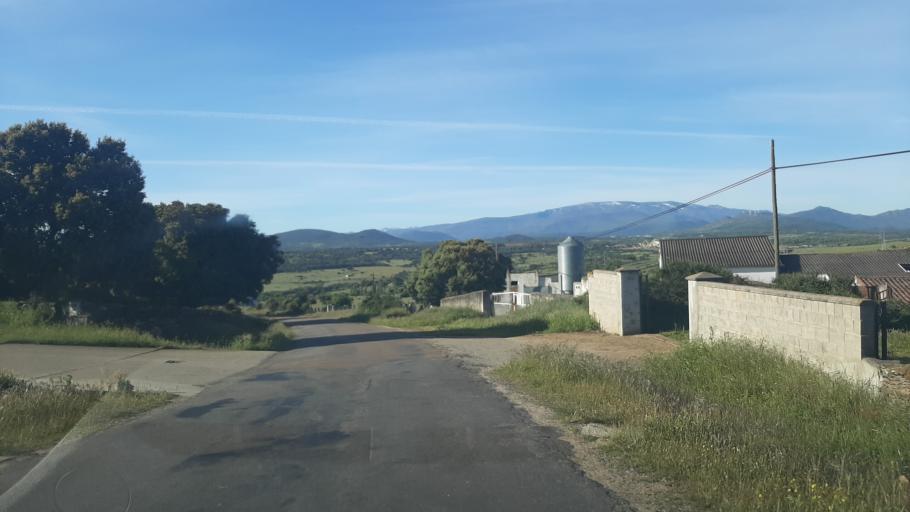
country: ES
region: Castille and Leon
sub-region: Provincia de Salamanca
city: Guijuelo
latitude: 40.5447
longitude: -5.6638
